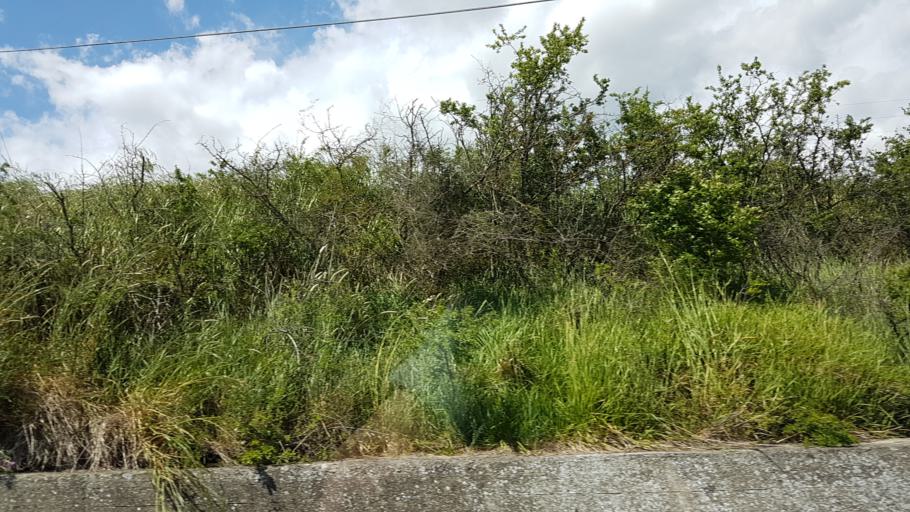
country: IT
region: Tuscany
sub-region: Province of Pisa
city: Orciano Pisano
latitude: 43.4521
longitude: 10.5156
